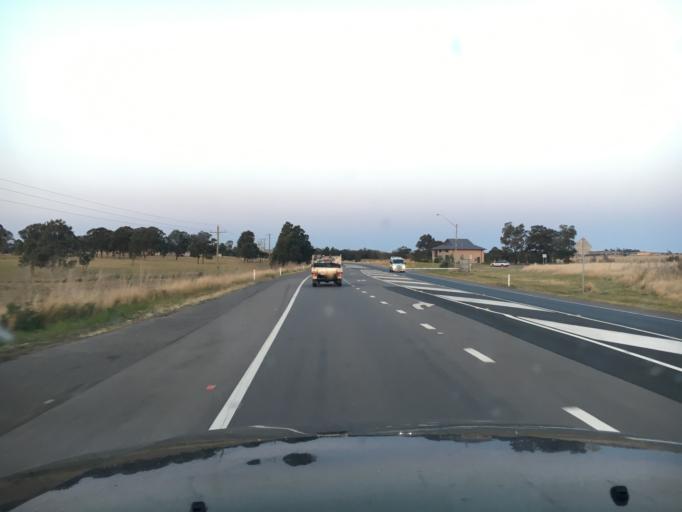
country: AU
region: New South Wales
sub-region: Cessnock
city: Greta
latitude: -32.7042
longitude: 151.4386
